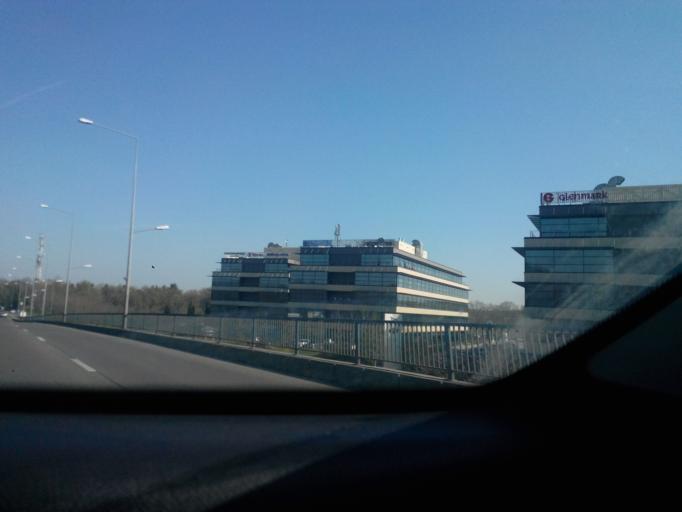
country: RO
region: Ilfov
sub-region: Comuna Otopeni
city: Otopeni
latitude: 44.5145
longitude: 26.0802
